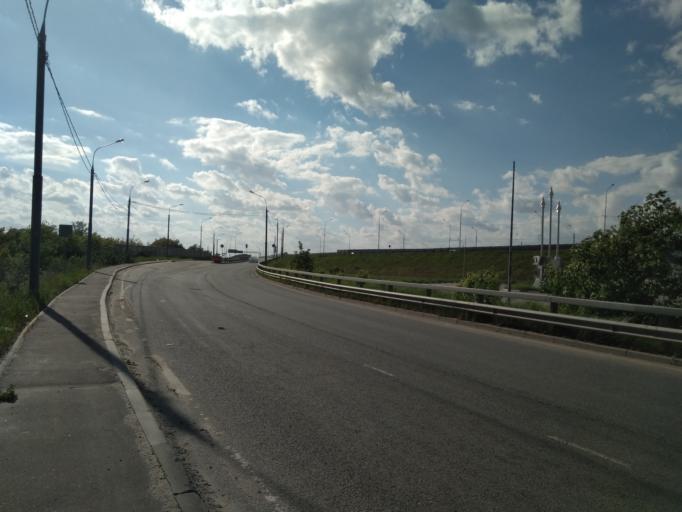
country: RU
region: Moskovskaya
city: Zhukovskiy
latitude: 55.5722
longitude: 38.1113
